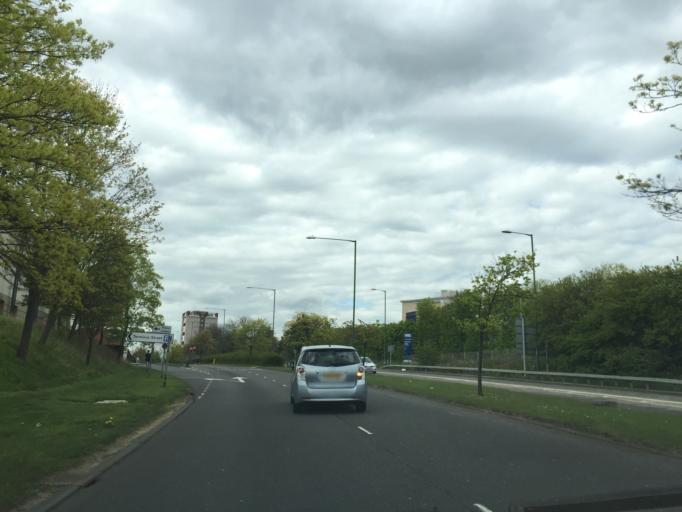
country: GB
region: England
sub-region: Essex
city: Harlow
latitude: 51.7683
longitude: 0.0975
